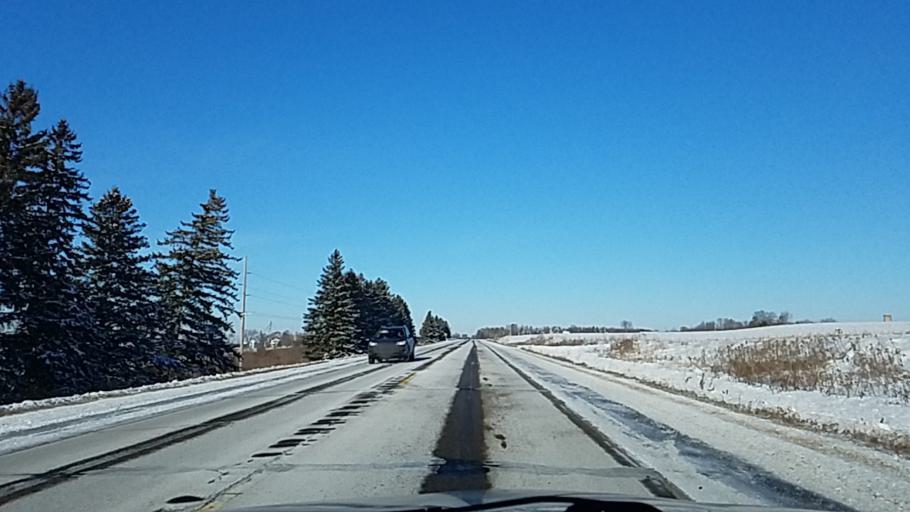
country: US
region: Wisconsin
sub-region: Saint Croix County
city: Roberts
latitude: 45.0448
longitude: -92.5373
